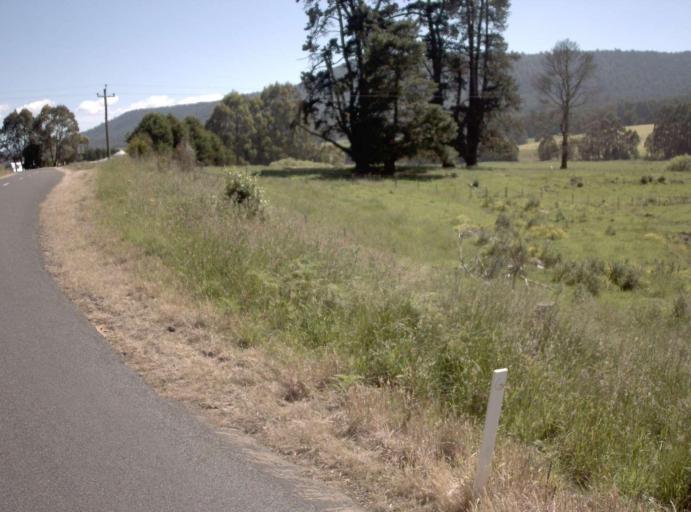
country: AU
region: New South Wales
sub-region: Bombala
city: Bombala
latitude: -37.1981
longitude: 148.7258
